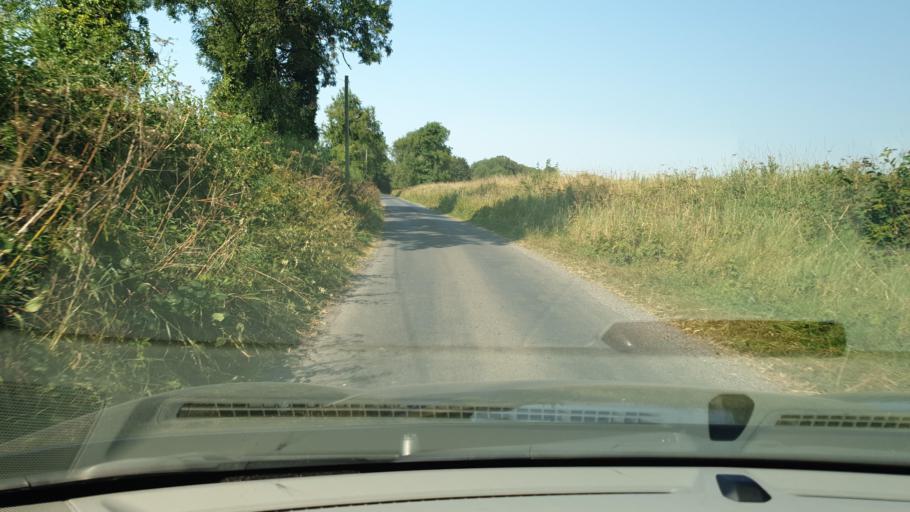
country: IE
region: Leinster
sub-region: An Mhi
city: Athboy
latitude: 53.6248
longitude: -6.9887
